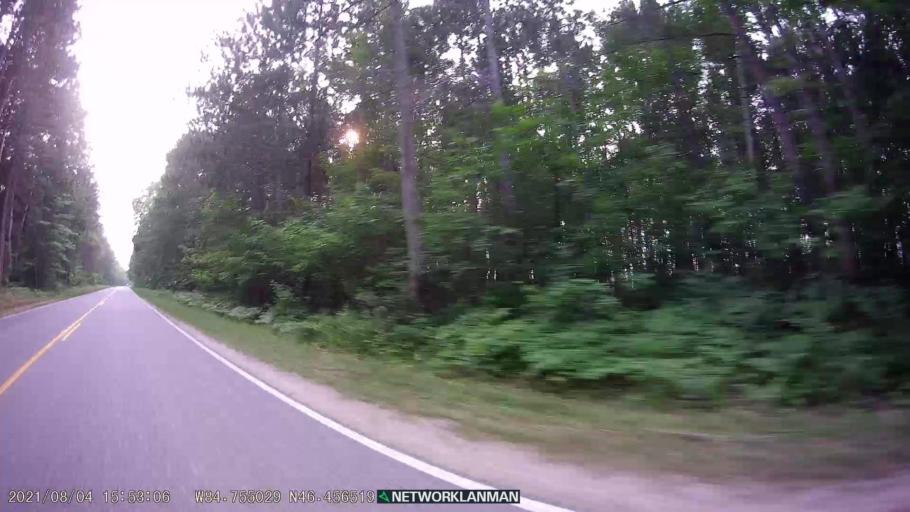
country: US
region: Michigan
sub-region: Chippewa County
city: Sault Ste. Marie
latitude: 46.4565
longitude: -84.7552
